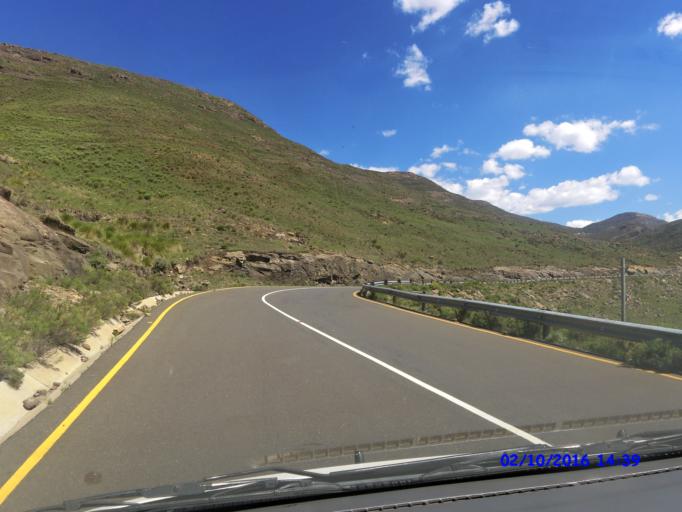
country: LS
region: Maseru
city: Nako
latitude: -29.5134
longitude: 28.0625
